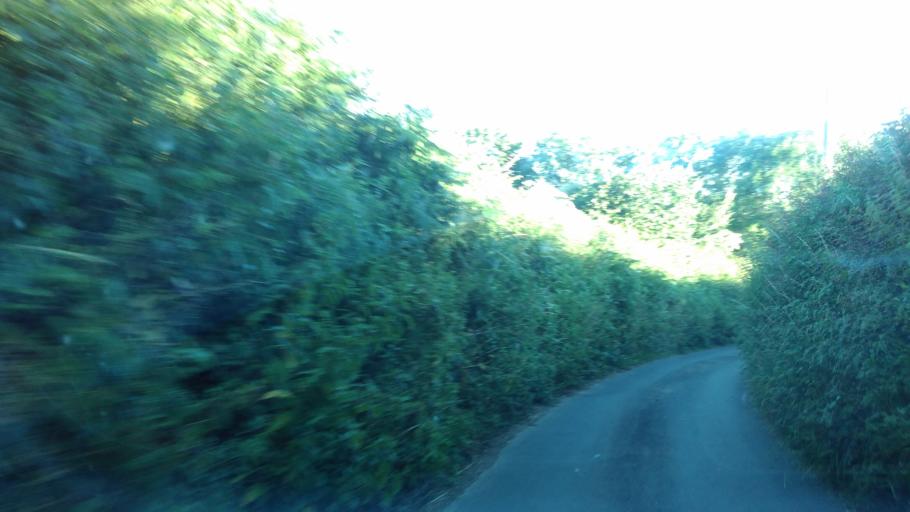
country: GB
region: England
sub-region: Kent
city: Chartham
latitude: 51.2460
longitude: 0.9951
